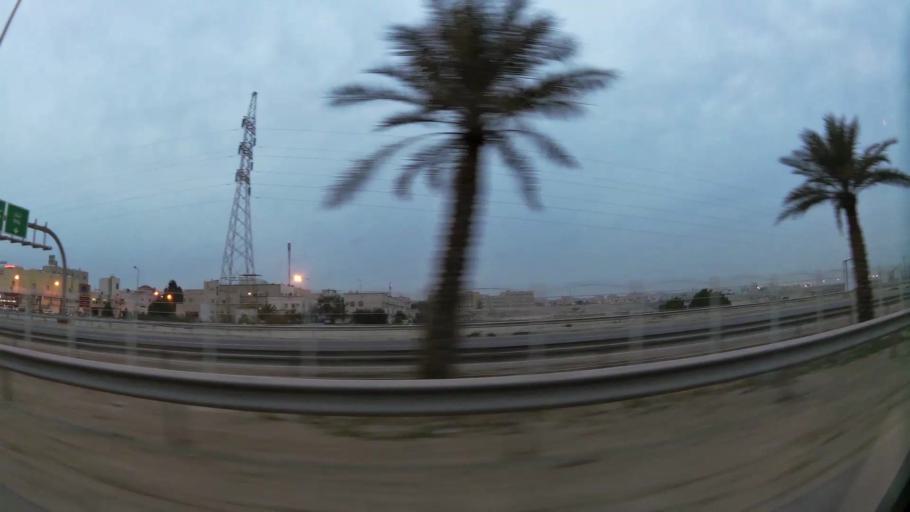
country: BH
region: Northern
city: Ar Rifa'
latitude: 26.1448
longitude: 50.5777
